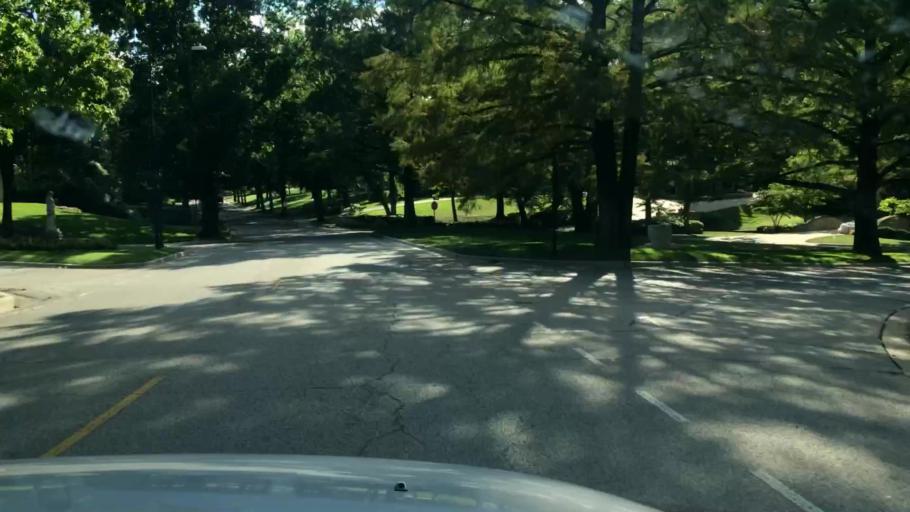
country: US
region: Kansas
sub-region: Johnson County
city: Mission Hills
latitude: 39.0105
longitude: -94.6199
